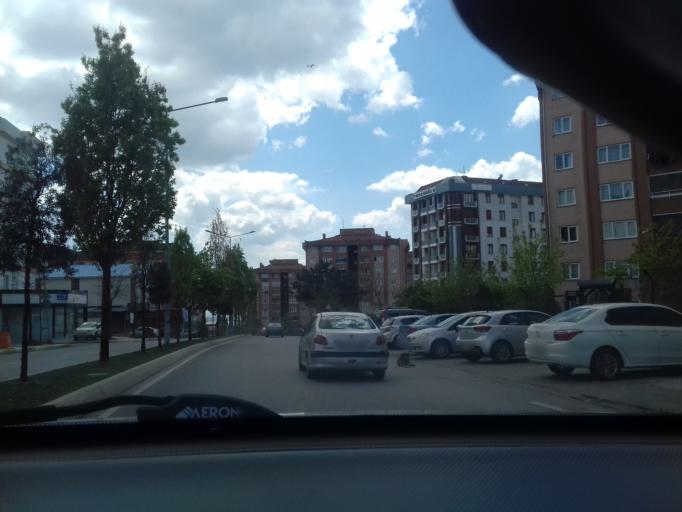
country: TR
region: Istanbul
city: Pendik
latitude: 40.9079
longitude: 29.2786
